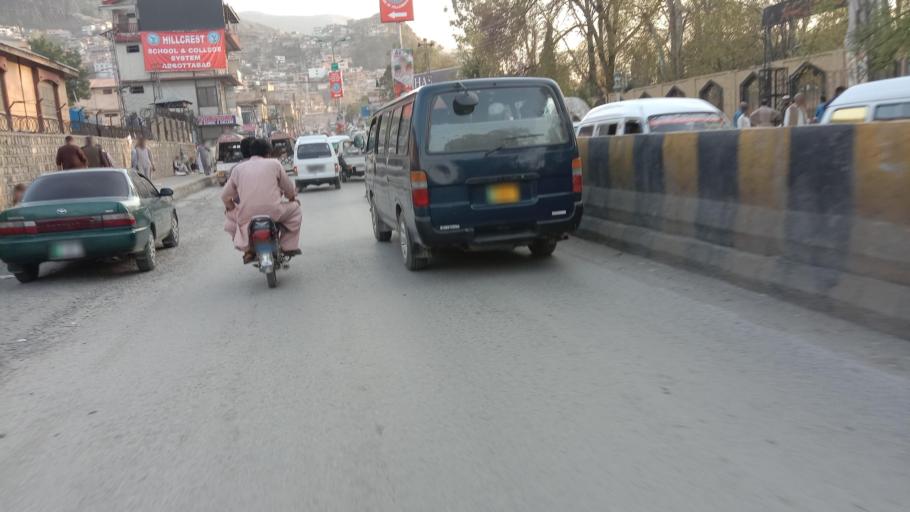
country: PK
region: Khyber Pakhtunkhwa
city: Abbottabad
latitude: 34.1448
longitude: 73.2149
